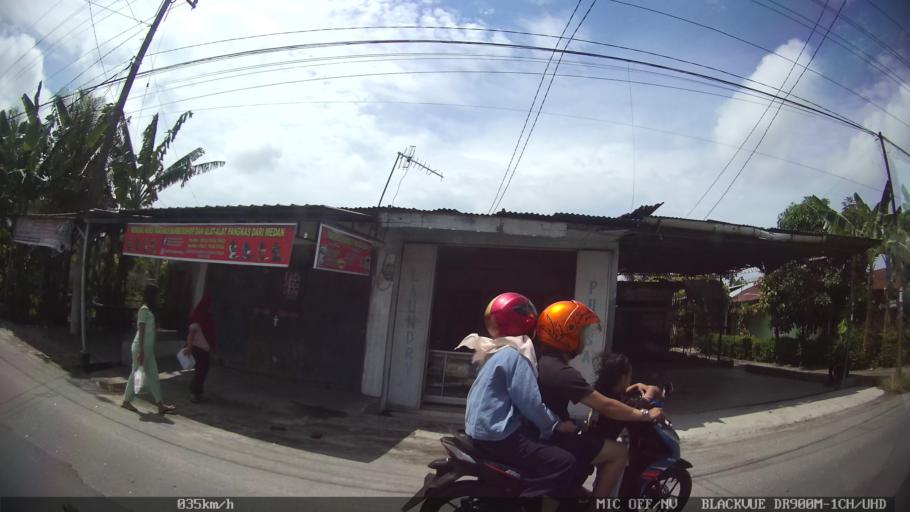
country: ID
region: North Sumatra
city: Percut
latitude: 3.6070
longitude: 98.7865
